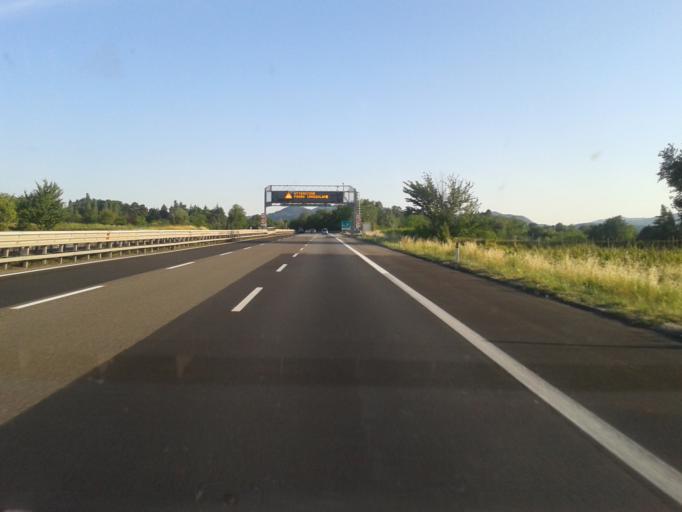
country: IT
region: Piedmont
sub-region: Provincia di Alessandria
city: Tagliolo Monferrato
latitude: 44.6464
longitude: 8.6610
